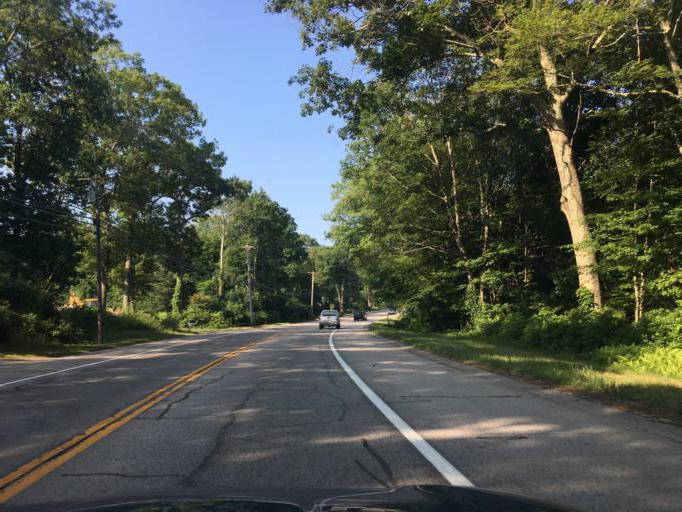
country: US
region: Rhode Island
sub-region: Washington County
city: Exeter
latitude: 41.5383
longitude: -71.5393
